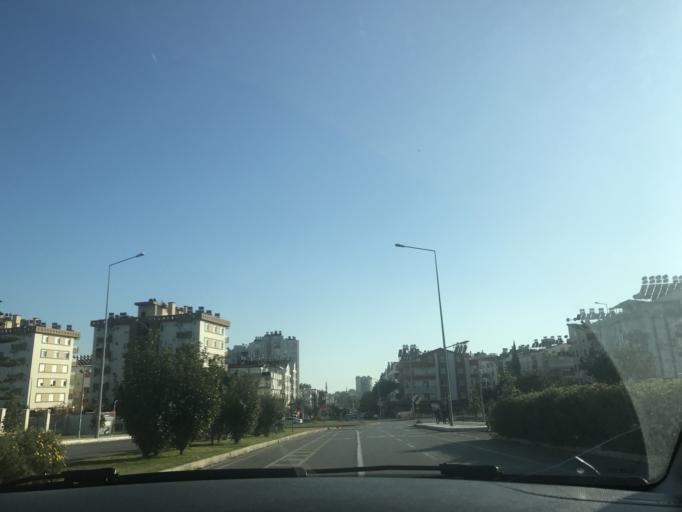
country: TR
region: Antalya
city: Antalya
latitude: 36.8889
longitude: 30.6463
